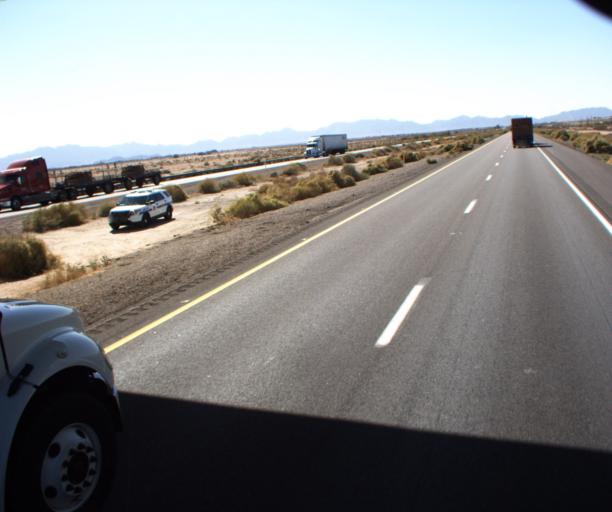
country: US
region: Arizona
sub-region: Yuma County
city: Wellton
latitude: 32.6746
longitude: -114.0735
